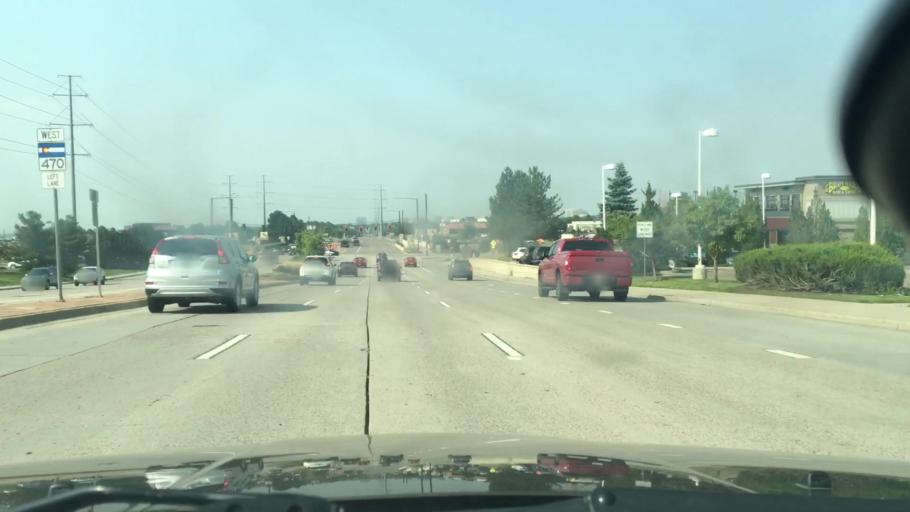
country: US
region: Colorado
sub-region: Douglas County
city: Acres Green
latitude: 39.5614
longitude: -104.9043
